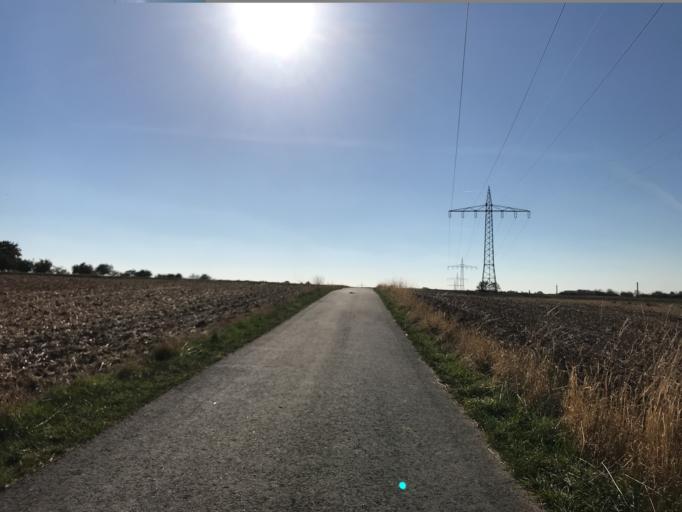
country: DE
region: Hesse
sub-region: Regierungsbezirk Darmstadt
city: Hochheim am Main
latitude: 50.0475
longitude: 8.3481
